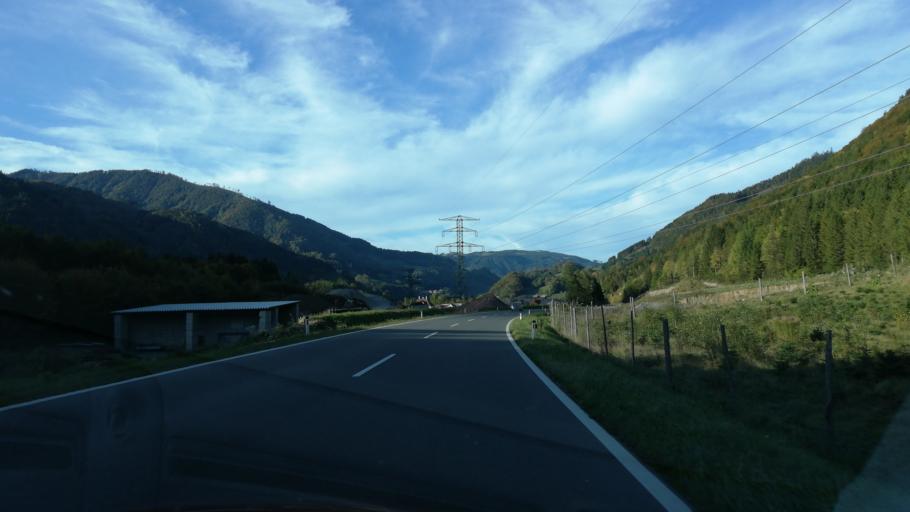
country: AT
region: Upper Austria
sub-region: Politischer Bezirk Steyr-Land
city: Weyer
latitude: 47.7944
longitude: 14.6461
